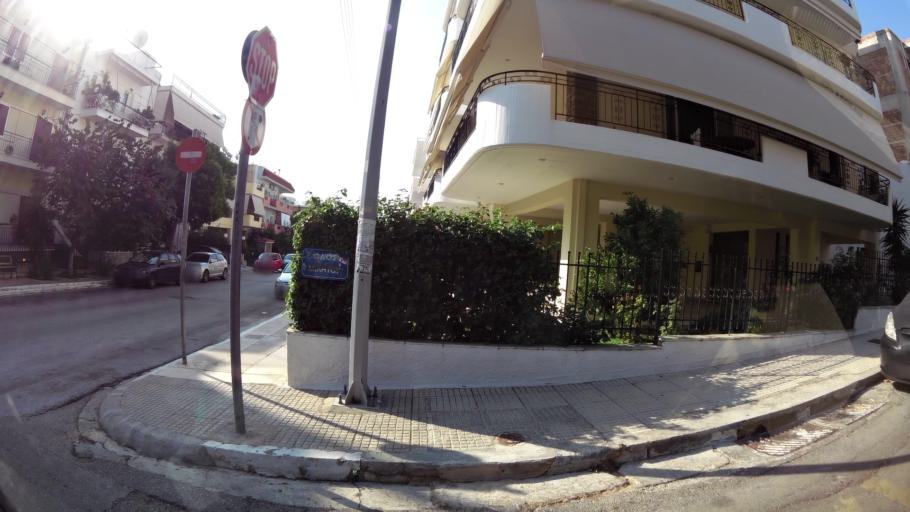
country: GR
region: Attica
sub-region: Nomarchia Athinas
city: Argyroupoli
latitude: 37.9059
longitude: 23.7572
